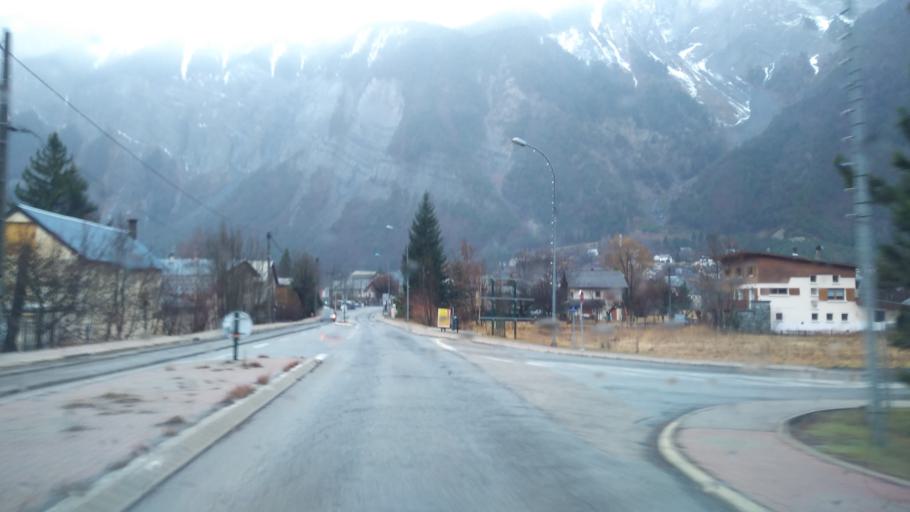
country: FR
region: Rhone-Alpes
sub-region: Departement de l'Isere
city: Huez
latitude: 45.0570
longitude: 6.0348
